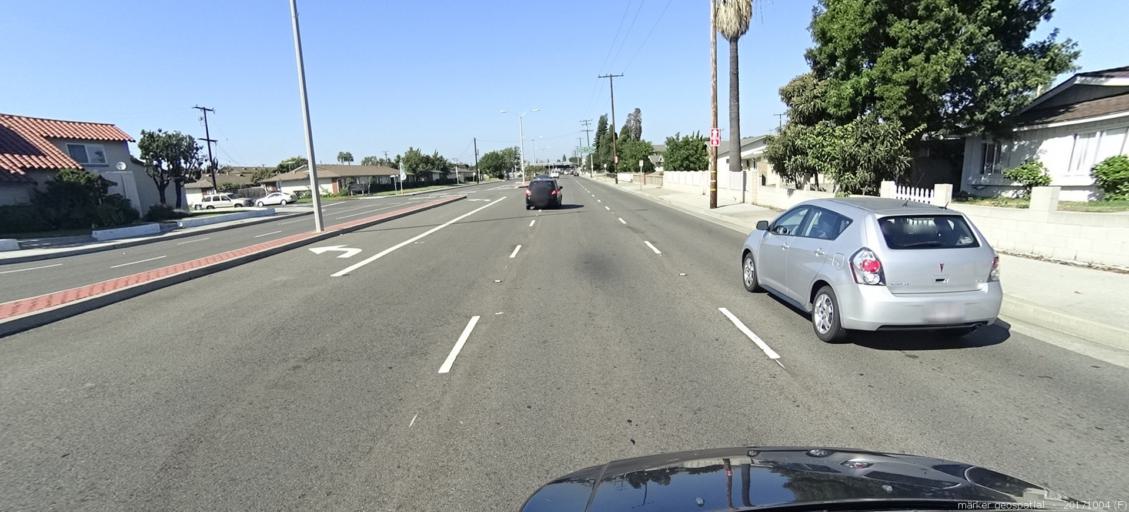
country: US
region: California
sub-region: Orange County
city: Midway City
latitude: 33.7614
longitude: -117.9724
